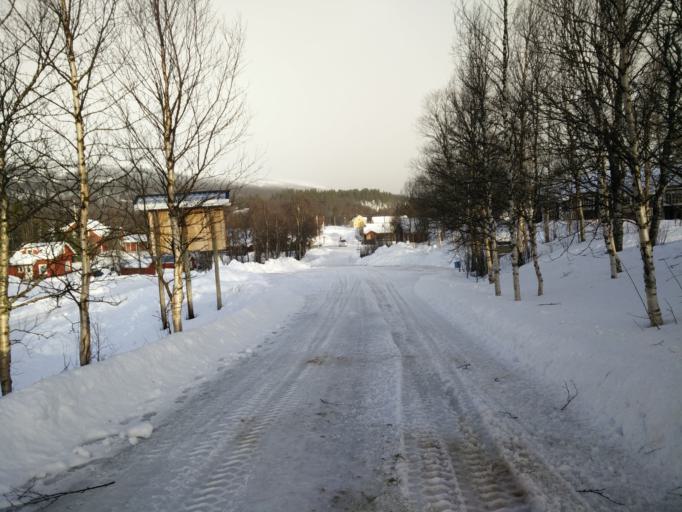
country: NO
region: Sor-Trondelag
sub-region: Tydal
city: Aas
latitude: 62.6400
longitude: 12.4180
